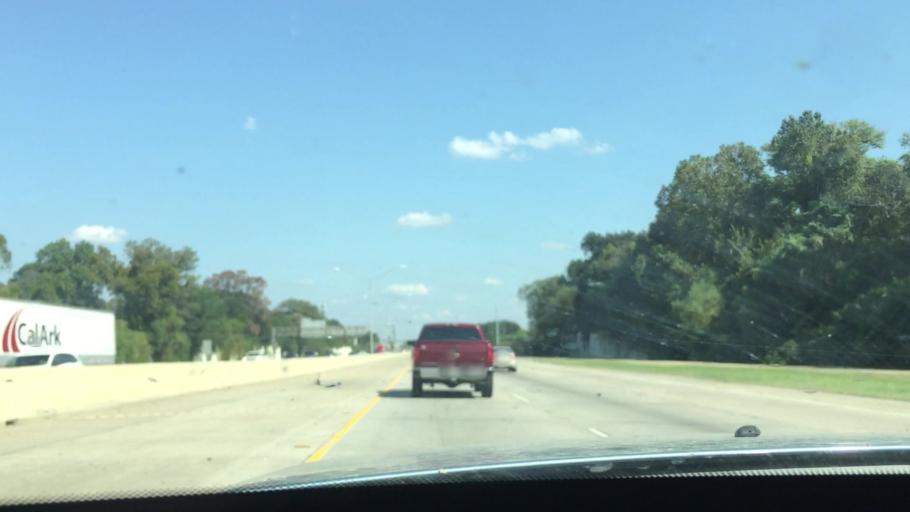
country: US
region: Louisiana
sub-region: East Baton Rouge Parish
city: Westminster
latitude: 30.4184
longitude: -91.1105
